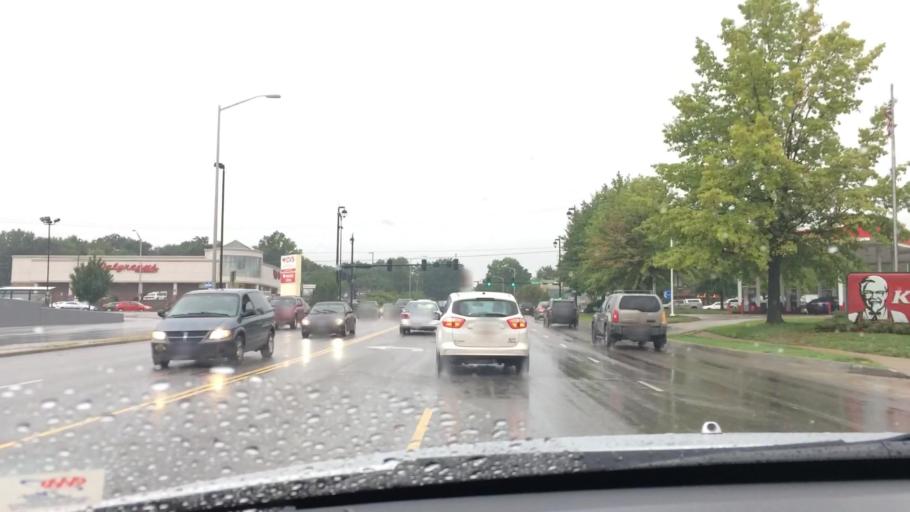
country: US
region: Kansas
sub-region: Johnson County
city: Overland Park
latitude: 38.9929
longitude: -94.6663
